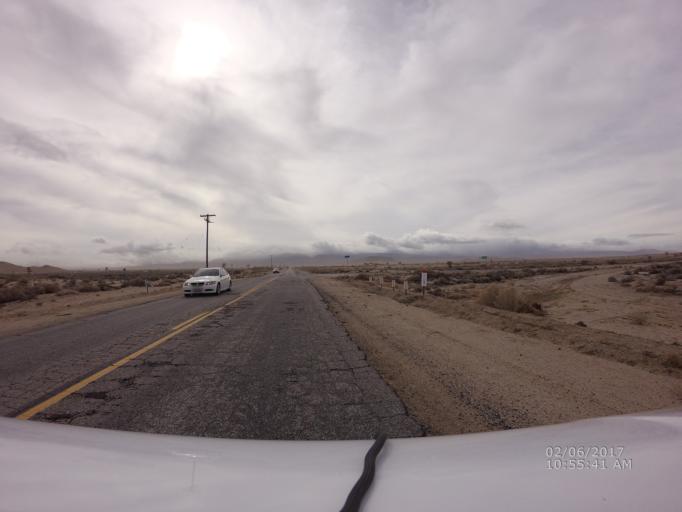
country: US
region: California
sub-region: Los Angeles County
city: Lake Los Angeles
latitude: 34.6170
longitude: -117.7028
